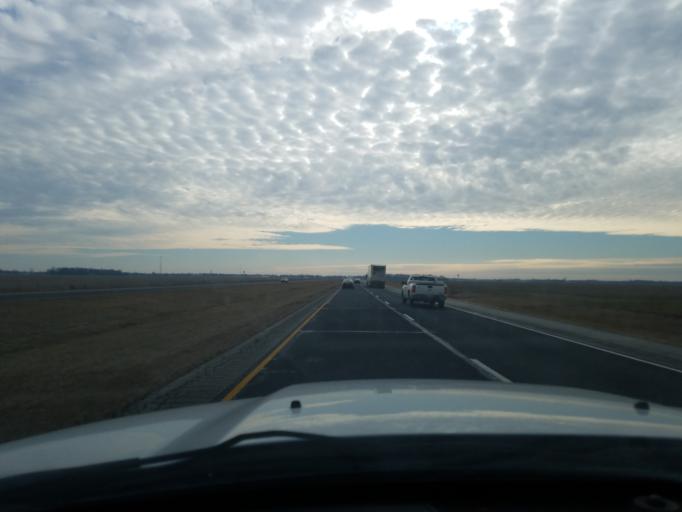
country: US
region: Indiana
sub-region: Huntington County
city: Markle
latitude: 40.8598
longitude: -85.3449
